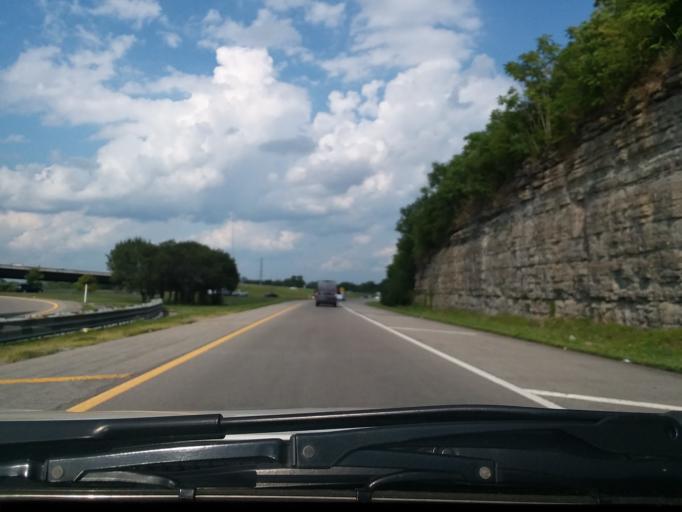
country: US
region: Tennessee
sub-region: Davidson County
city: Nashville
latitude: 36.2375
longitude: -86.7410
